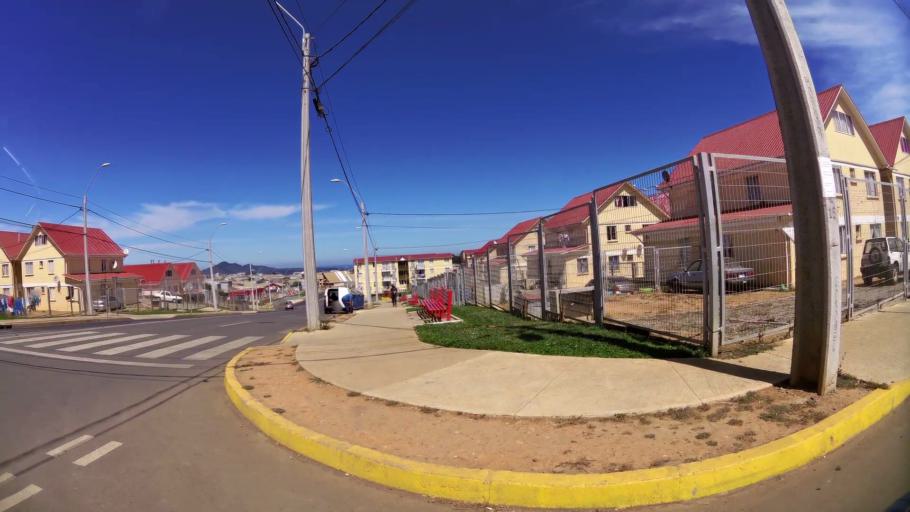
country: CL
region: Biobio
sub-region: Provincia de Concepcion
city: Talcahuano
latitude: -36.7108
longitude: -73.1322
